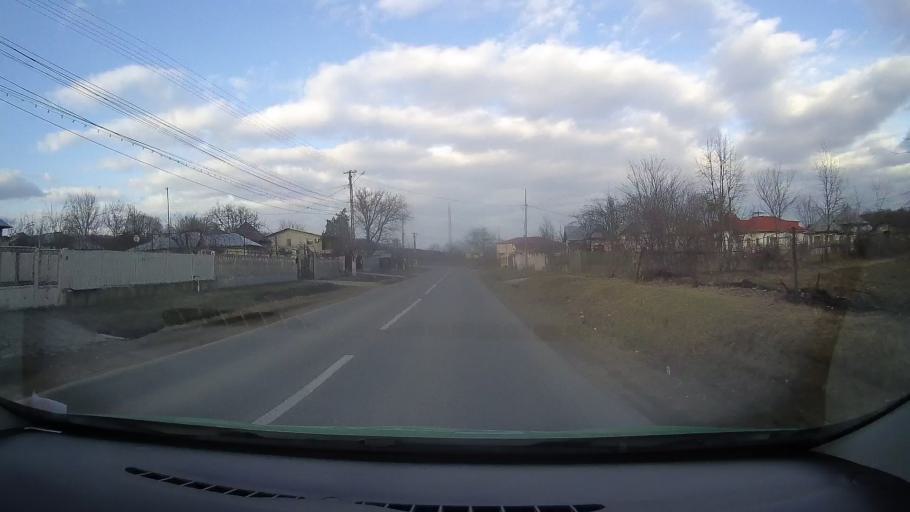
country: RO
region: Dambovita
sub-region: Comuna Gura Ocnitei
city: Gura Ocnitei
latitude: 44.9398
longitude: 25.5799
